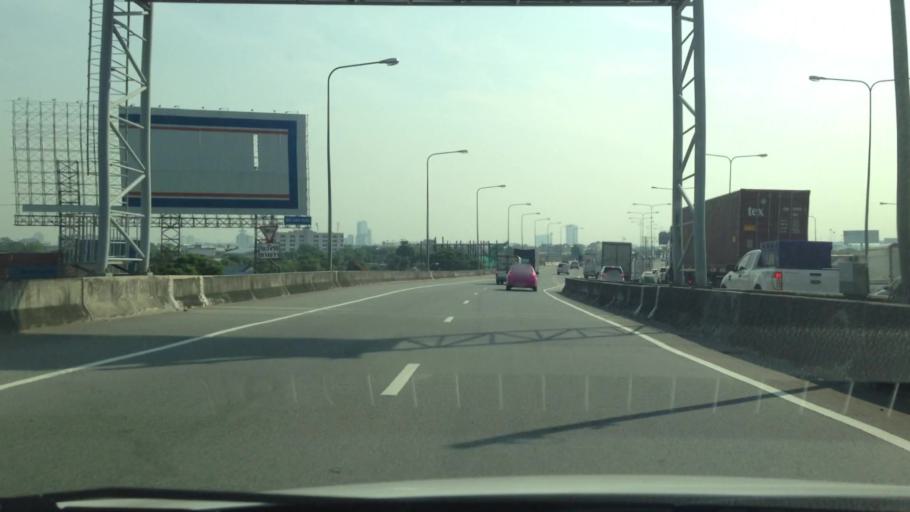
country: TH
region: Samut Prakan
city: Phra Pradaeng
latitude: 13.6390
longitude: 100.5530
